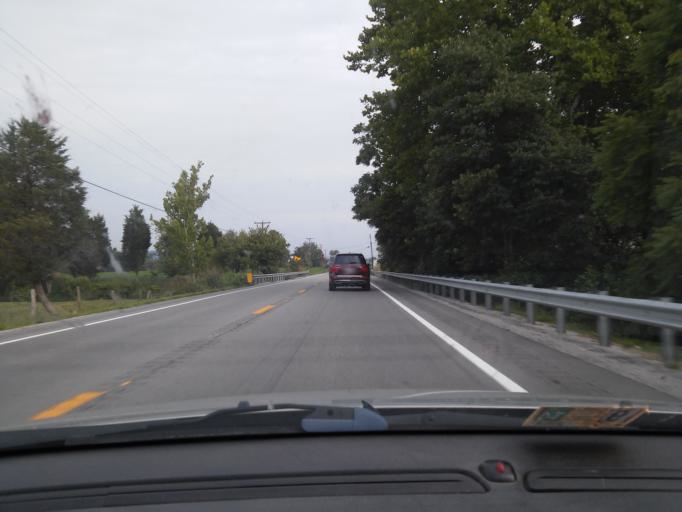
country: US
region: West Virginia
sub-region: Putnam County
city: Buffalo
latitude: 38.7191
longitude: -81.9696
